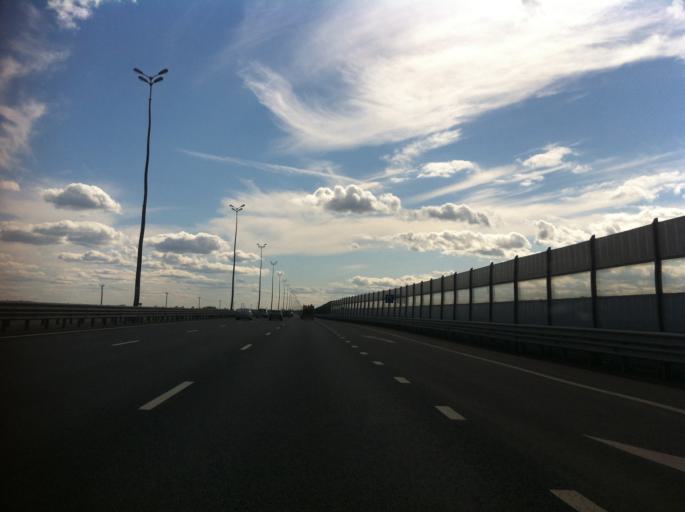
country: RU
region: Leningrad
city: Maloye Verevo
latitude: 59.6434
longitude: 30.2233
